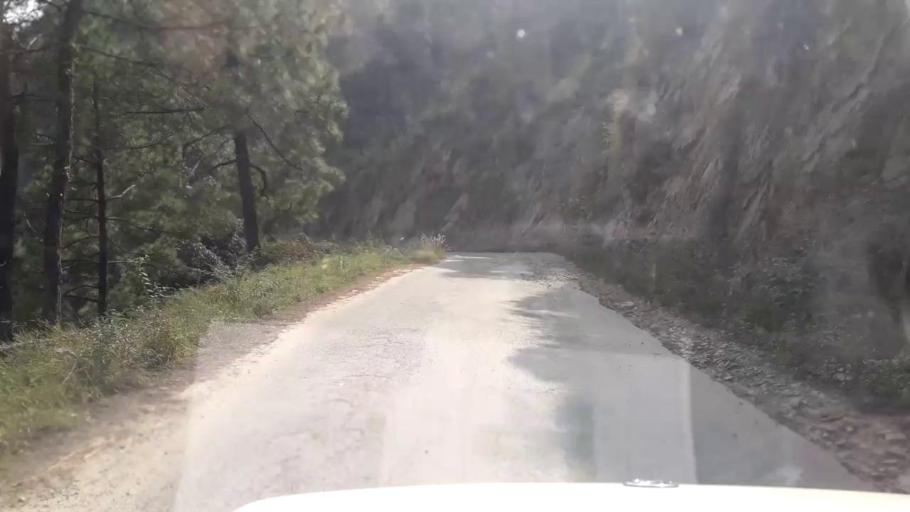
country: IN
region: Himachal Pradesh
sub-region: Shimla
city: Shimla
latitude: 31.0587
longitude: 77.1558
